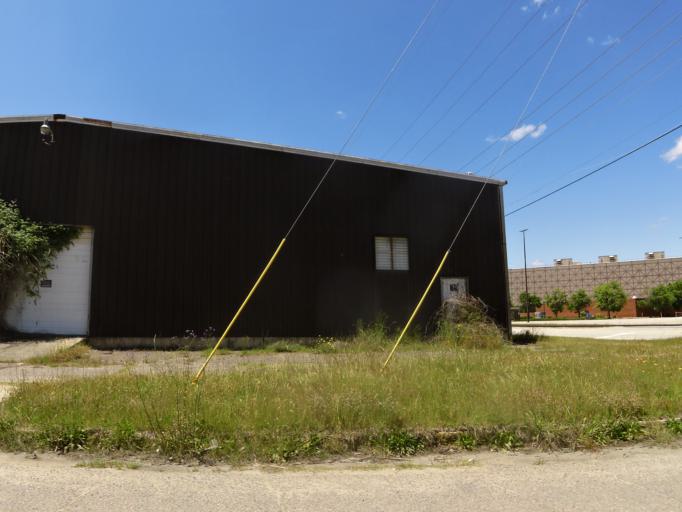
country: US
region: Georgia
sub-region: Richmond County
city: Augusta
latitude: 33.4681
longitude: -81.9656
